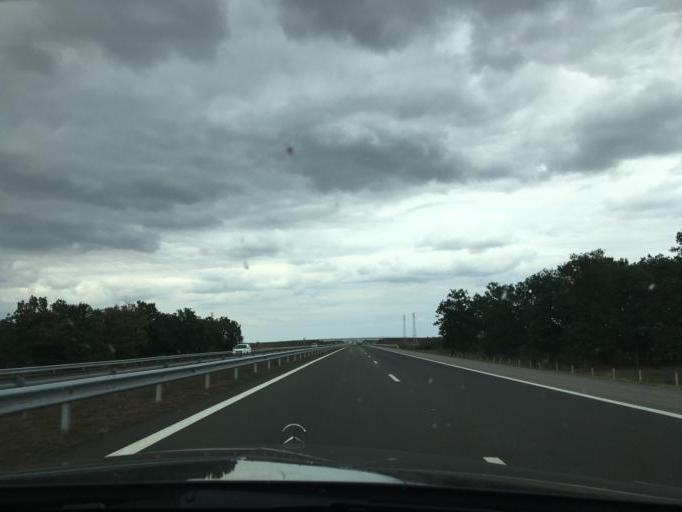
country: BG
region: Stara Zagora
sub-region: Obshtina Stara Zagora
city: Stara Zagora
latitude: 42.3629
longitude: 25.7670
